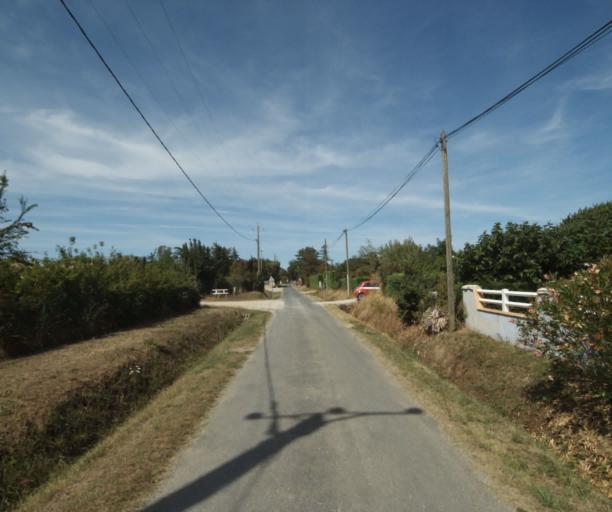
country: FR
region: Midi-Pyrenees
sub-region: Departement de la Haute-Garonne
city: Revel
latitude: 43.5085
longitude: 2.0327
